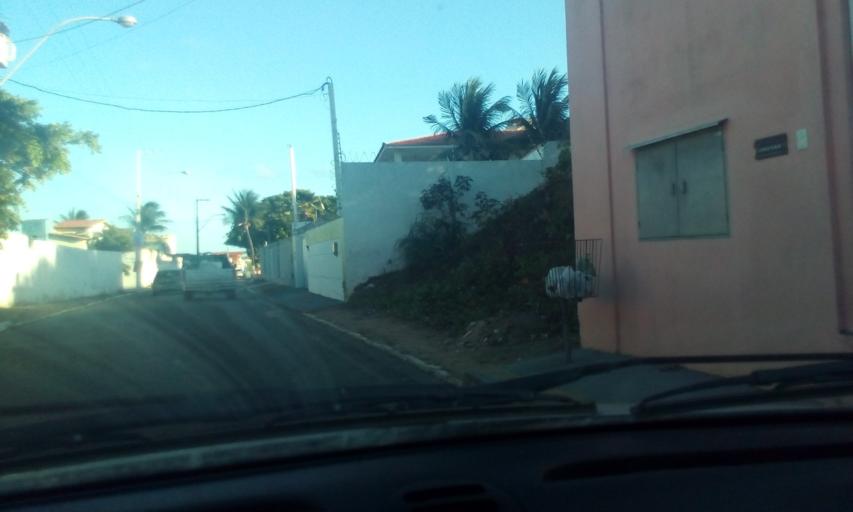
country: BR
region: Rio Grande do Norte
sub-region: Parnamirim
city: Parnamirim
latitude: -5.9598
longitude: -35.1505
